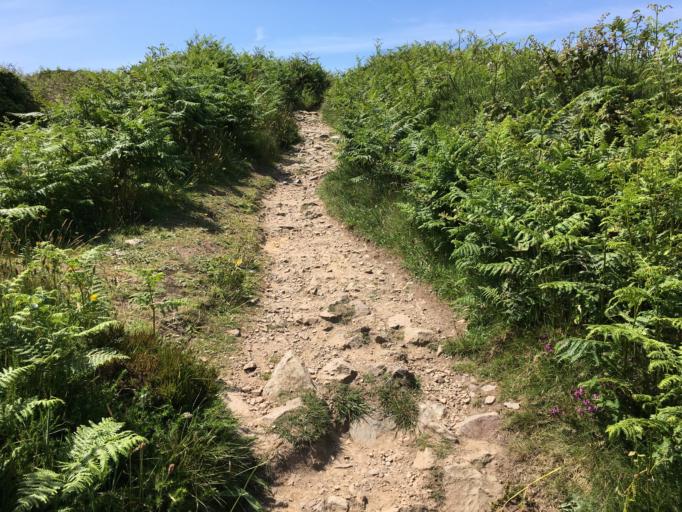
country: GB
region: England
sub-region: Cornwall
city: Saint Agnes
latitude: 50.3208
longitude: -5.2129
